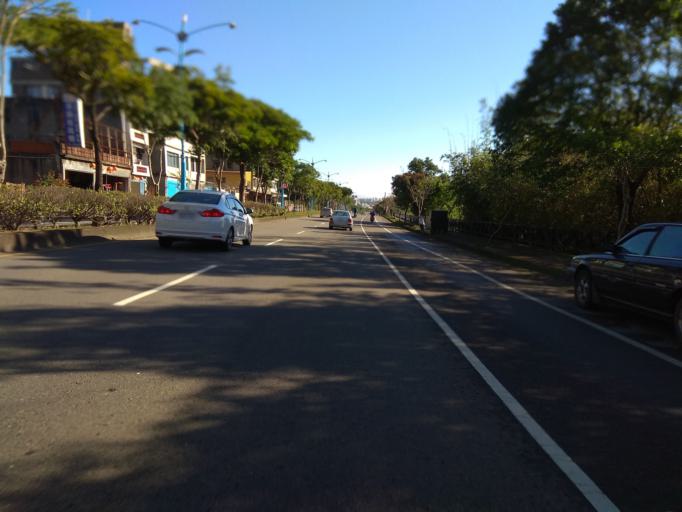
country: TW
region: Taiwan
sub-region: Hsinchu
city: Zhubei
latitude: 24.9050
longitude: 121.1305
